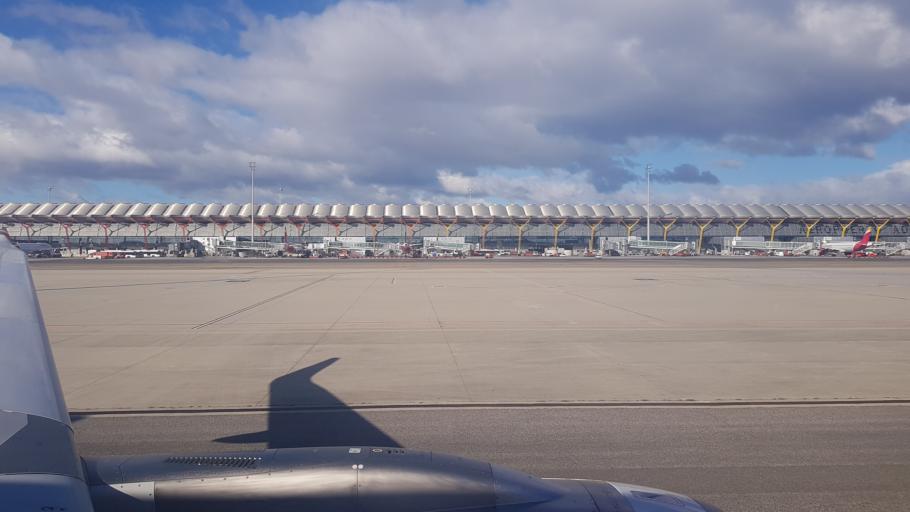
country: ES
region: Madrid
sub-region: Provincia de Madrid
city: Barajas de Madrid
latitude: 40.4884
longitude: -3.5865
